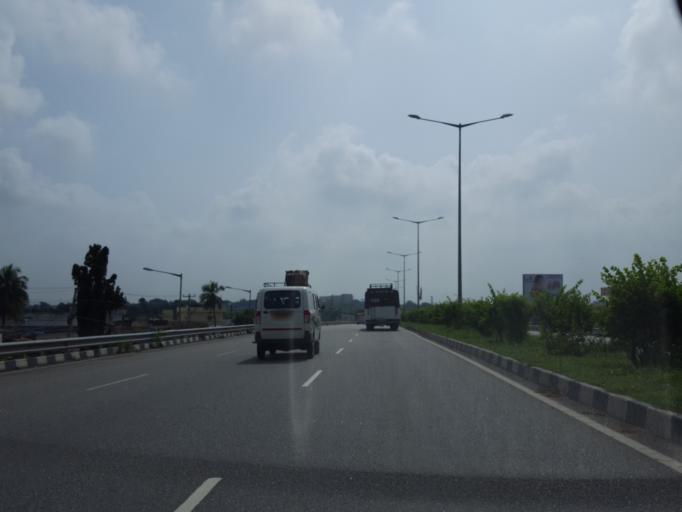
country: IN
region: Telangana
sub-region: Nalgonda
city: Gudur
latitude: 17.2606
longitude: 78.8442
